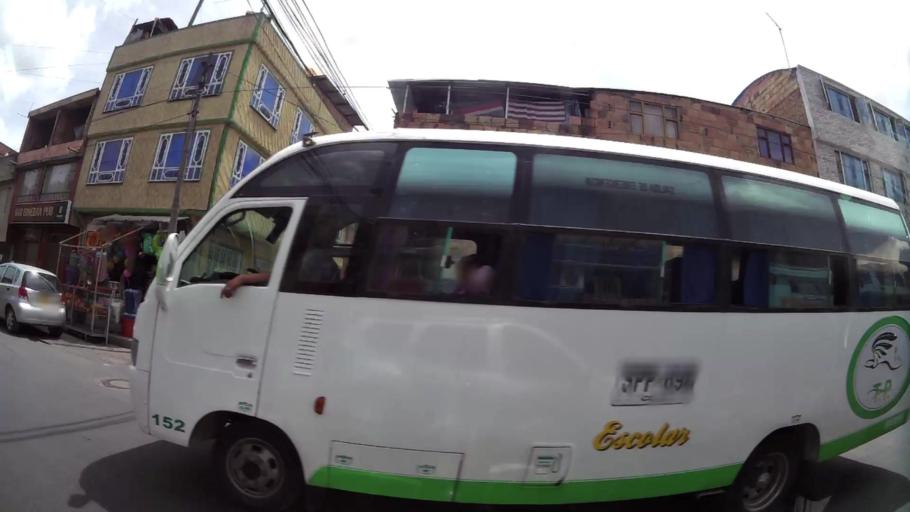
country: CO
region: Cundinamarca
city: Soacha
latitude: 4.6418
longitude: -74.1606
